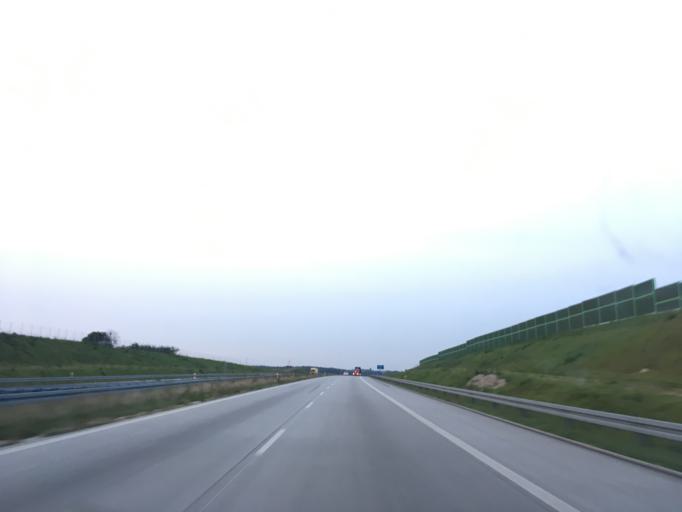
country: PL
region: Lodz Voivodeship
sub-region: Powiat zgierski
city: Strykow
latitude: 51.8554
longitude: 19.6595
